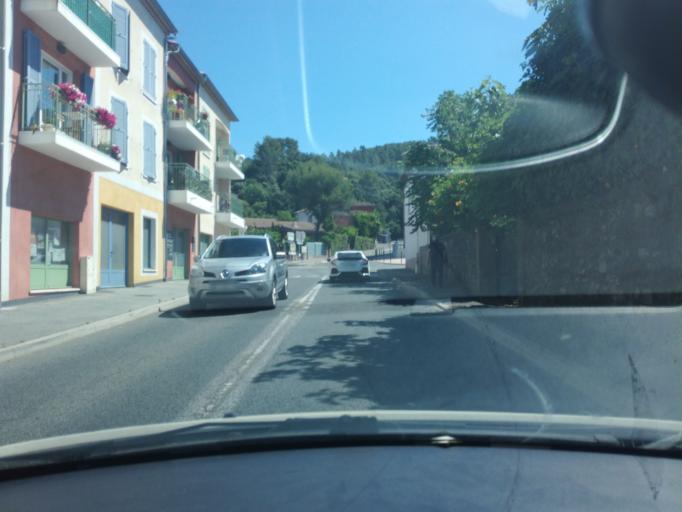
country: FR
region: Provence-Alpes-Cote d'Azur
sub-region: Departement du Var
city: Taradeau
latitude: 43.4545
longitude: 6.4267
